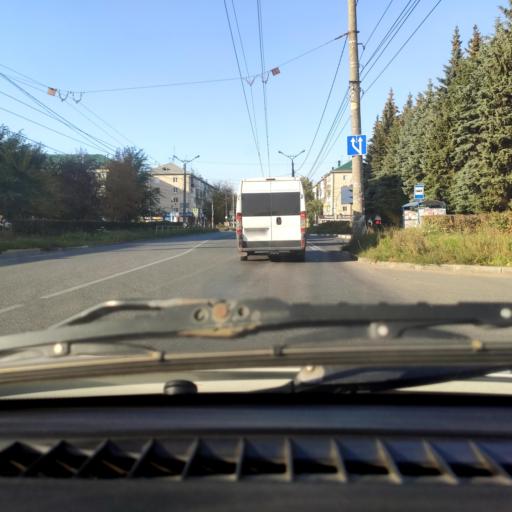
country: RU
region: Samara
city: Tol'yatti
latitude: 53.5212
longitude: 49.4152
